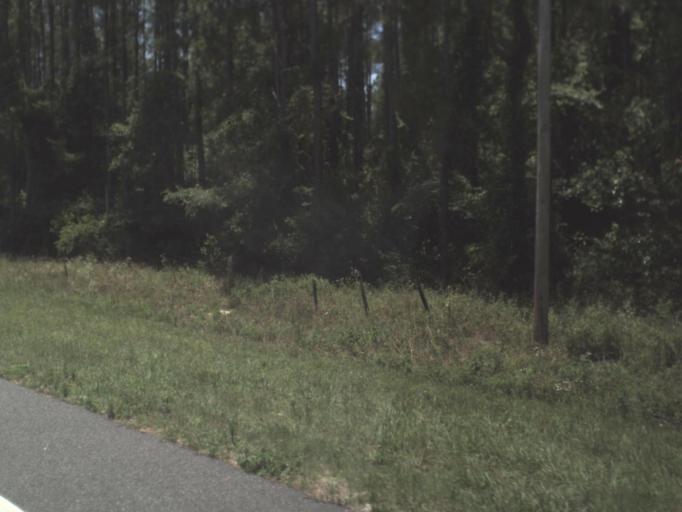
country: US
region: Florida
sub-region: Lafayette County
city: Mayo
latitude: 29.9462
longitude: -82.9488
